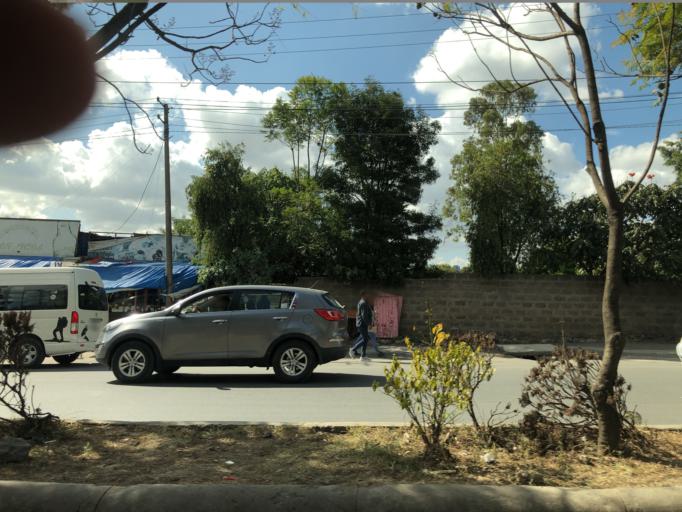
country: ET
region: Adis Abeba
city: Addis Ababa
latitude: 8.9971
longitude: 38.7790
